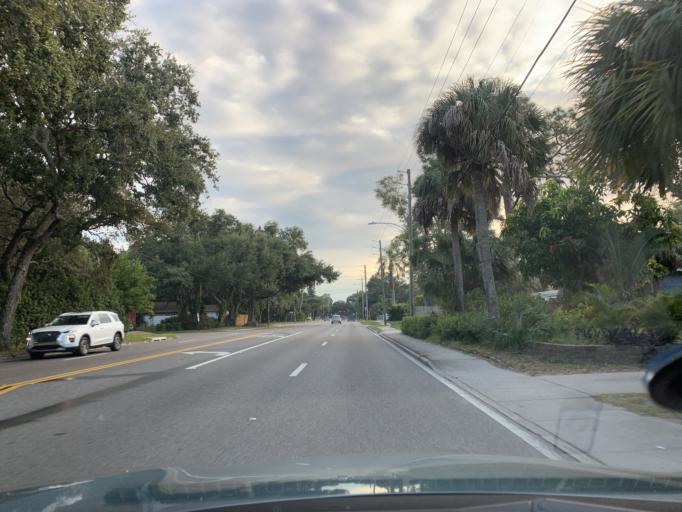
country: US
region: Florida
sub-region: Pinellas County
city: Bay Pines
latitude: 27.7966
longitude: -82.7539
